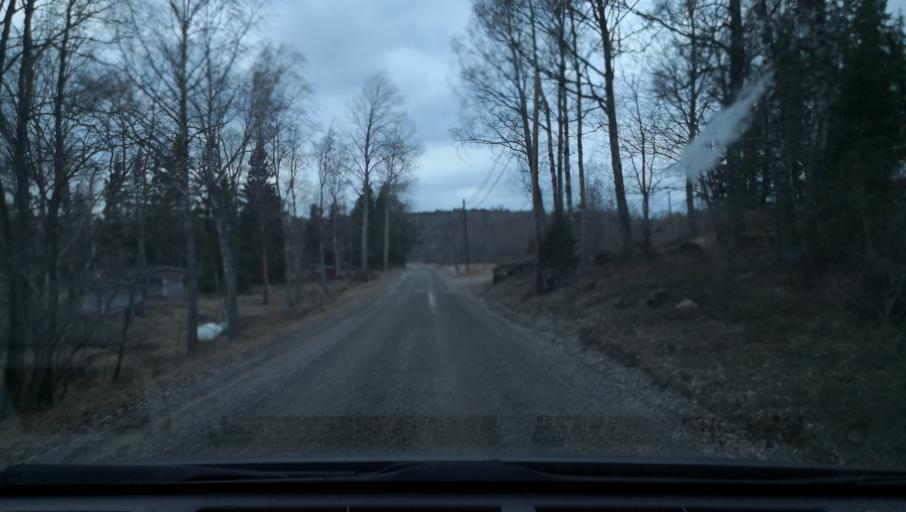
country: SE
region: Vaestmanland
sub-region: Kopings Kommun
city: Kolsva
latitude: 59.5977
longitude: 15.7147
